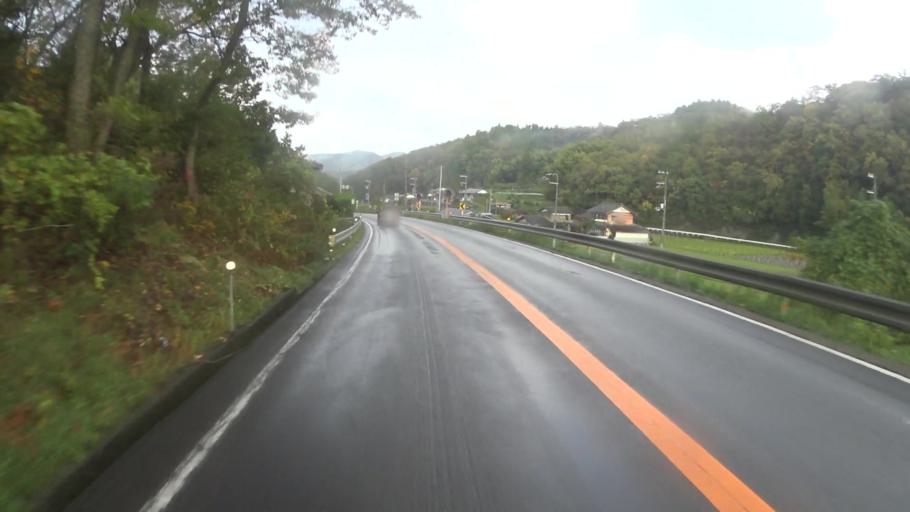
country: JP
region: Kyoto
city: Ayabe
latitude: 35.1829
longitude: 135.3444
